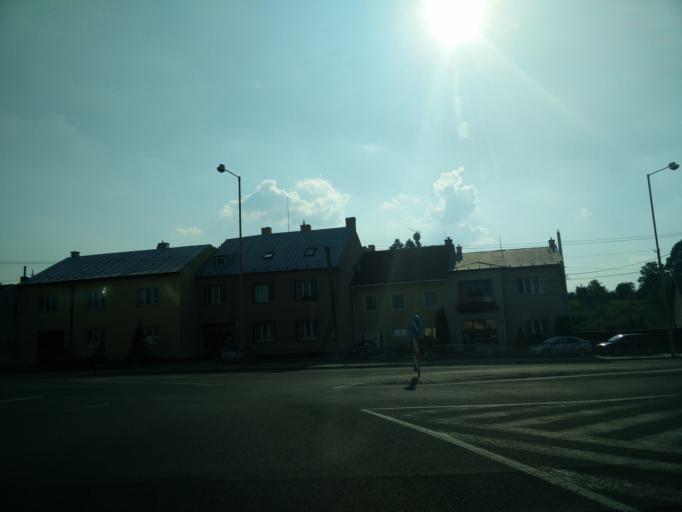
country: SK
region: Zilinsky
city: Rajec
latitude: 49.0902
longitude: 18.6334
